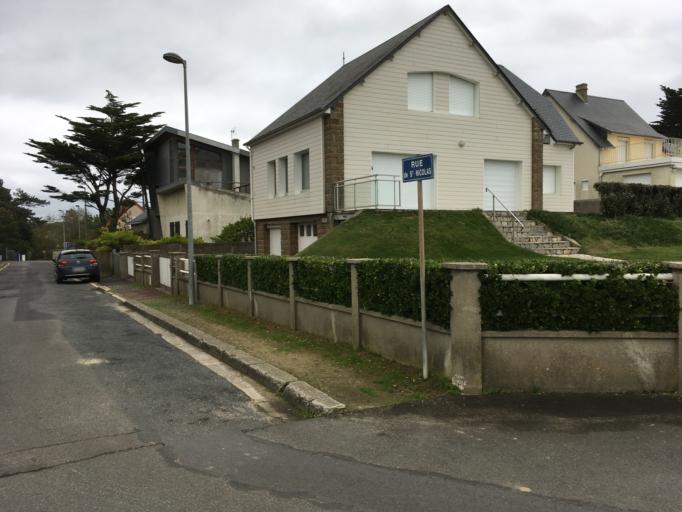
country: FR
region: Lower Normandy
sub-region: Departement de la Manche
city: Saint-Pair-sur-Mer
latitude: 48.7960
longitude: -1.5699
